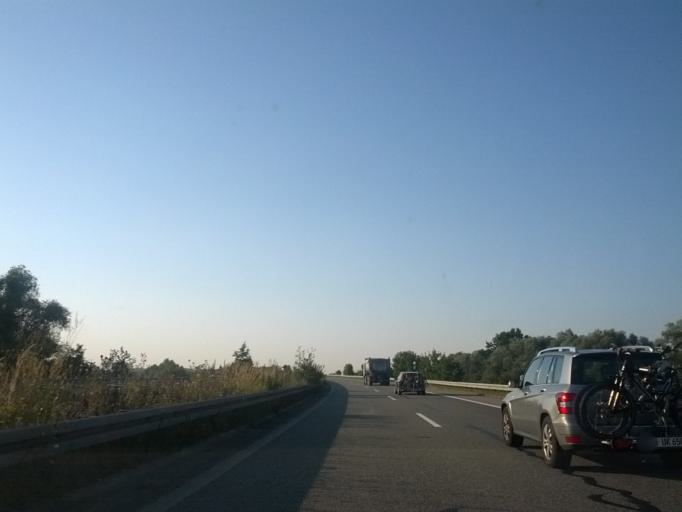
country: DE
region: Mecklenburg-Vorpommern
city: Wendorf
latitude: 54.2709
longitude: 13.0810
